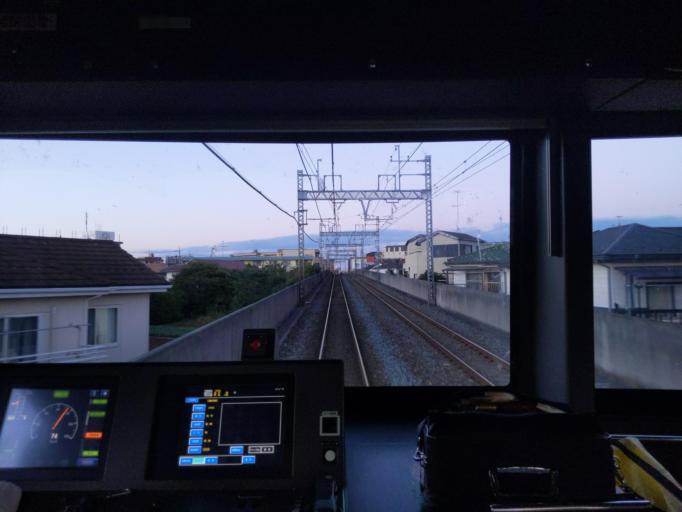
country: JP
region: Chiba
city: Kashiwa
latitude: 35.8520
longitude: 139.9661
